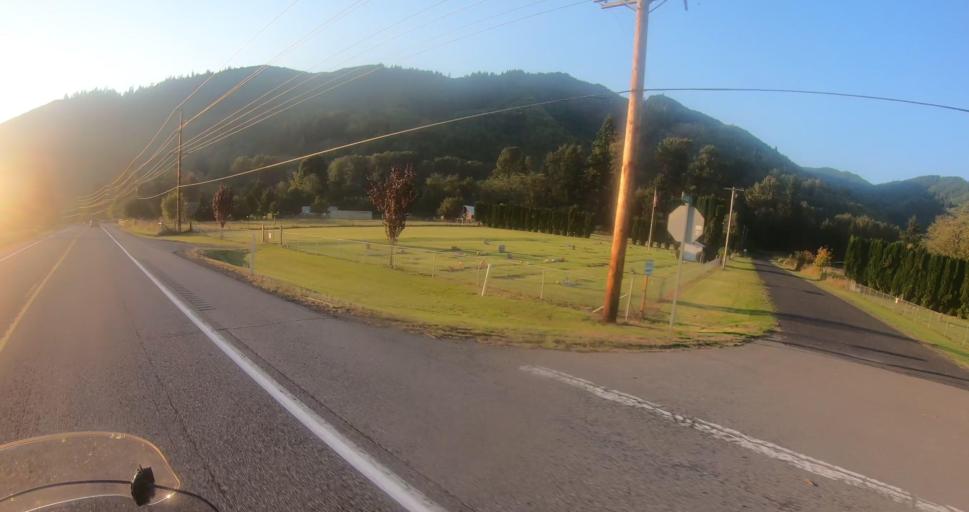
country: US
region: Washington
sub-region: Lewis County
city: Morton
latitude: 46.5477
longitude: -122.0696
